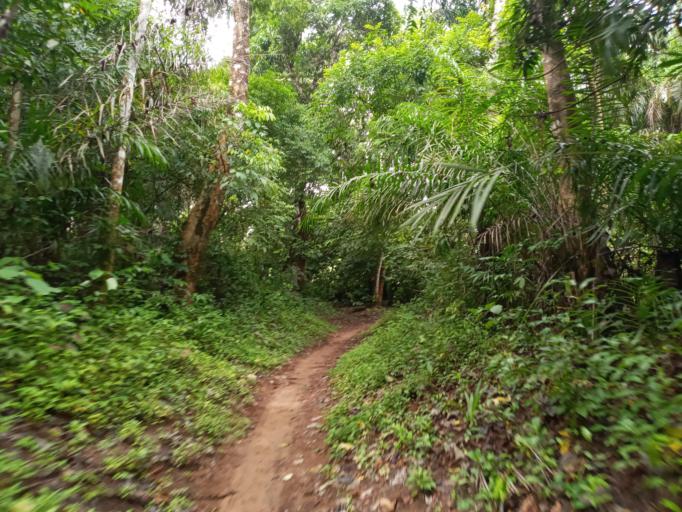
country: SL
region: Southern Province
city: Bonthe
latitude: 7.5113
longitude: -12.5489
